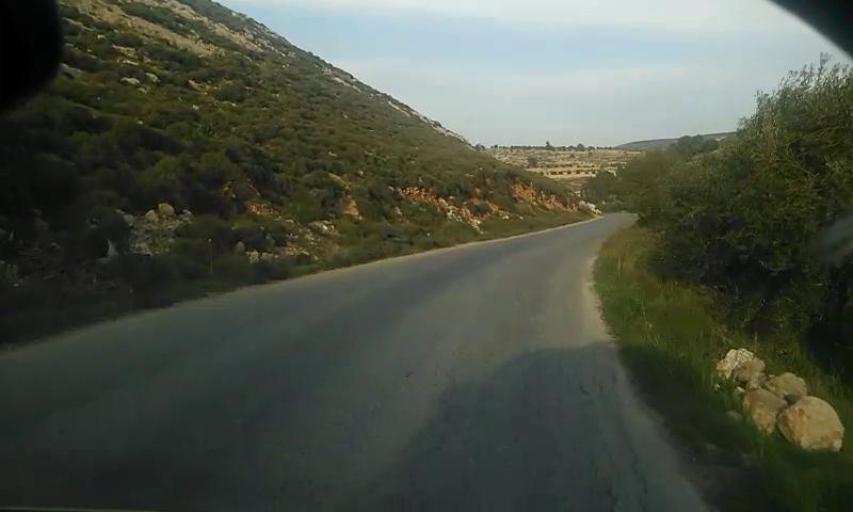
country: PS
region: West Bank
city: Ash Shuyukh
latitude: 31.5937
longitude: 35.1704
